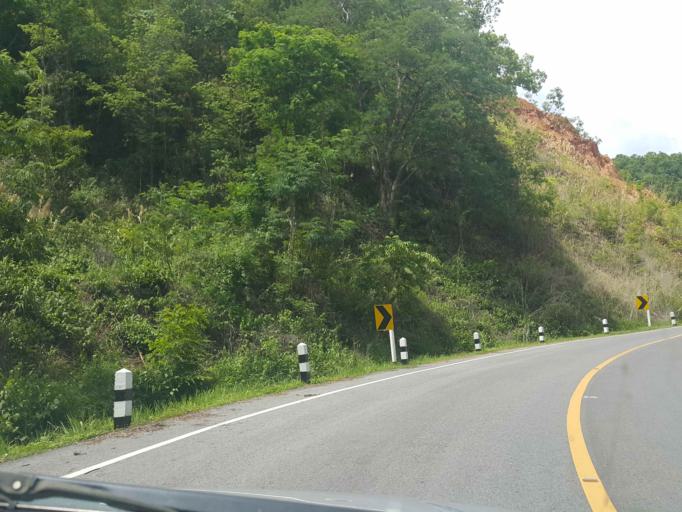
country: TH
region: Nan
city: Ban Luang
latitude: 18.8738
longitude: 100.4852
